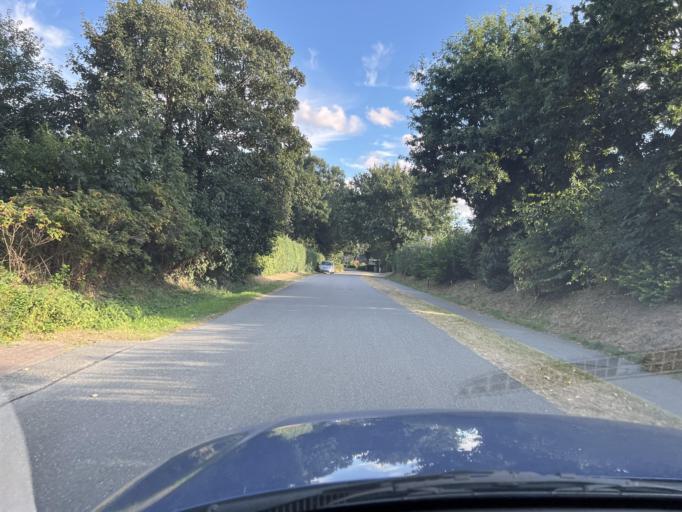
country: DE
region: Schleswig-Holstein
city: Wesseln
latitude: 54.2057
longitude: 9.0751
